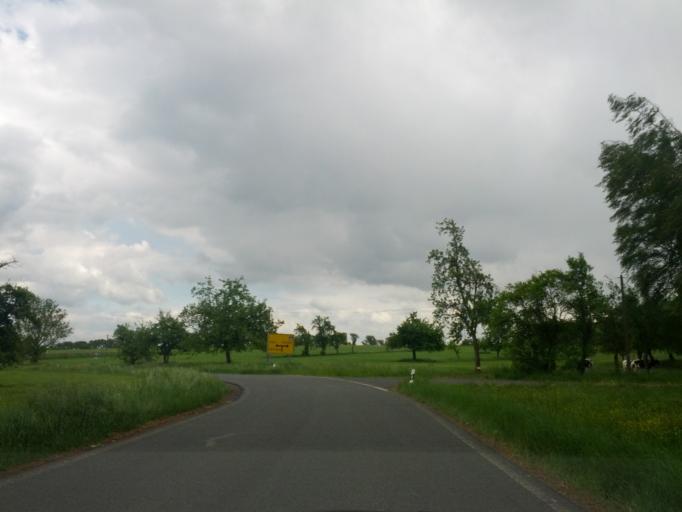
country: DE
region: Thuringia
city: Friedrichswerth
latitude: 50.9892
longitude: 10.5401
